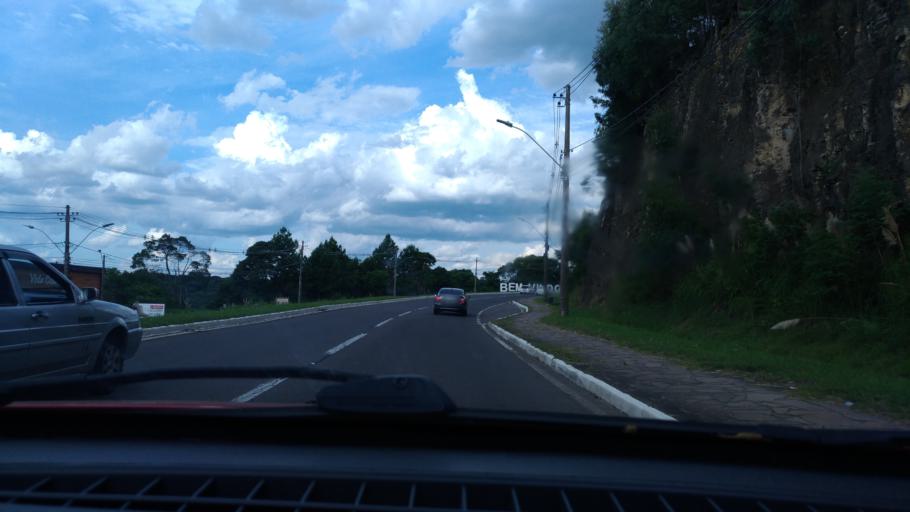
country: BR
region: Rio Grande do Sul
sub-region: Canela
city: Canela
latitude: -29.3598
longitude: -50.8426
